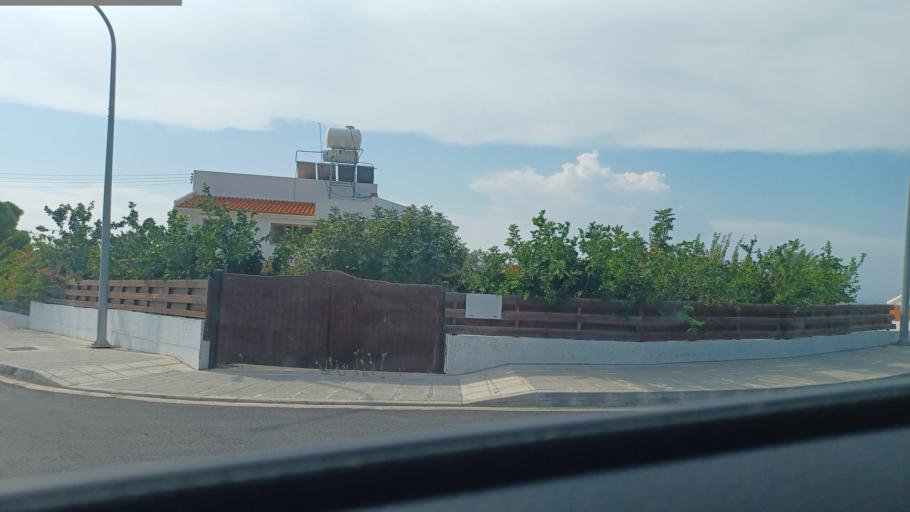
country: CY
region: Pafos
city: Pegeia
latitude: 34.8663
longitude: 32.3831
